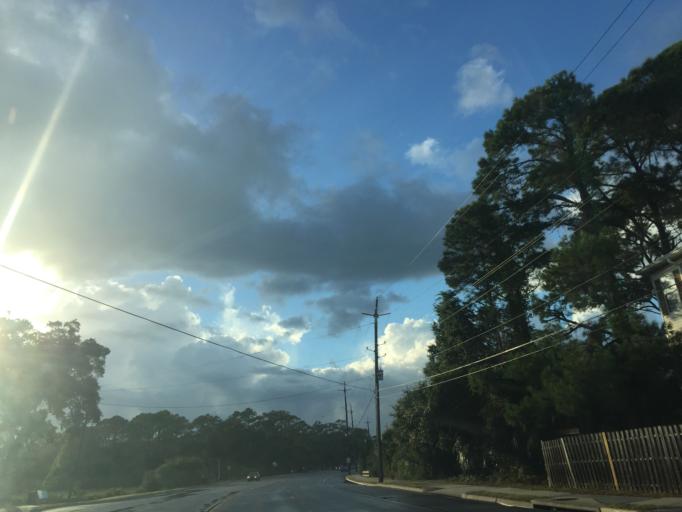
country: US
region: Georgia
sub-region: Chatham County
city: Tybee Island
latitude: 32.0140
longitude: -80.8460
